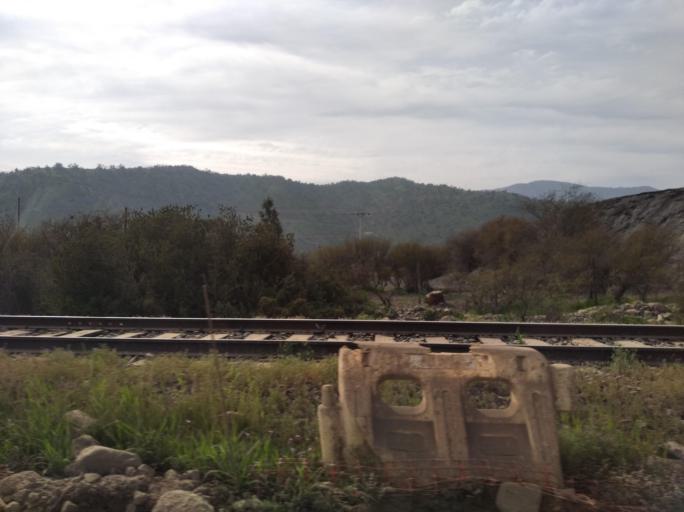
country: CL
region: Santiago Metropolitan
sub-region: Provincia de Chacabuco
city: Lampa
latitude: -33.1048
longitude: -70.9294
